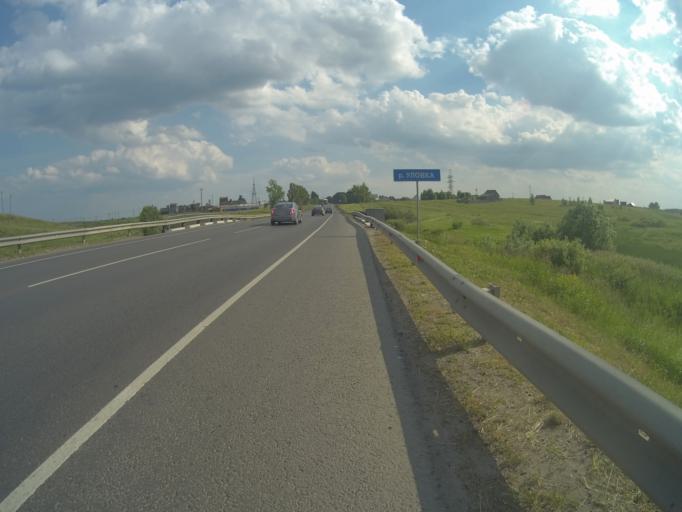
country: RU
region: Vladimir
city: Suzdal'
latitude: 56.3326
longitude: 40.4727
